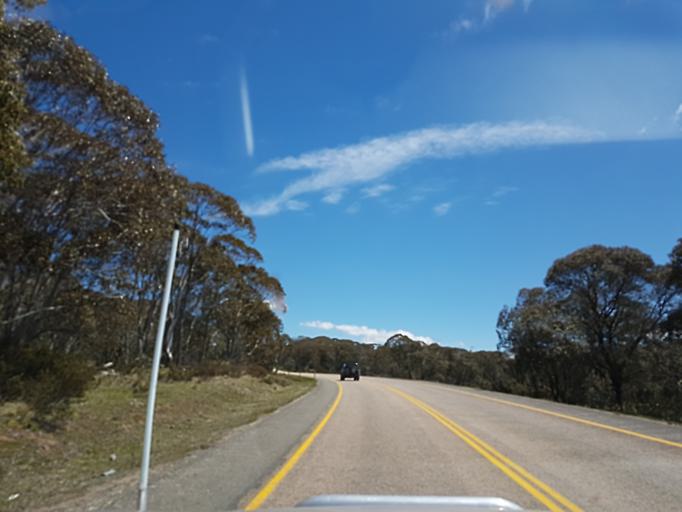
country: AU
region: Victoria
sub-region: Alpine
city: Mount Beauty
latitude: -37.0305
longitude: 147.2960
